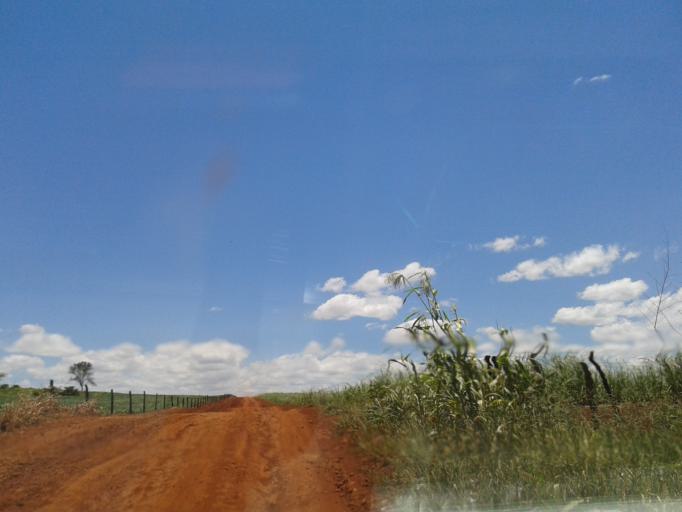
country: BR
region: Minas Gerais
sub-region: Centralina
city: Centralina
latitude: -18.6713
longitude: -49.2309
